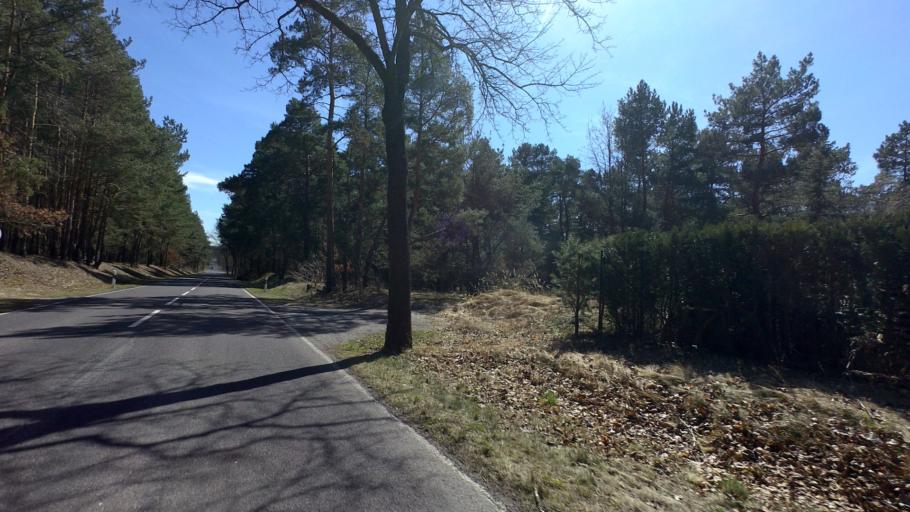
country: DE
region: Brandenburg
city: Teupitz
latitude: 52.1269
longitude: 13.6306
